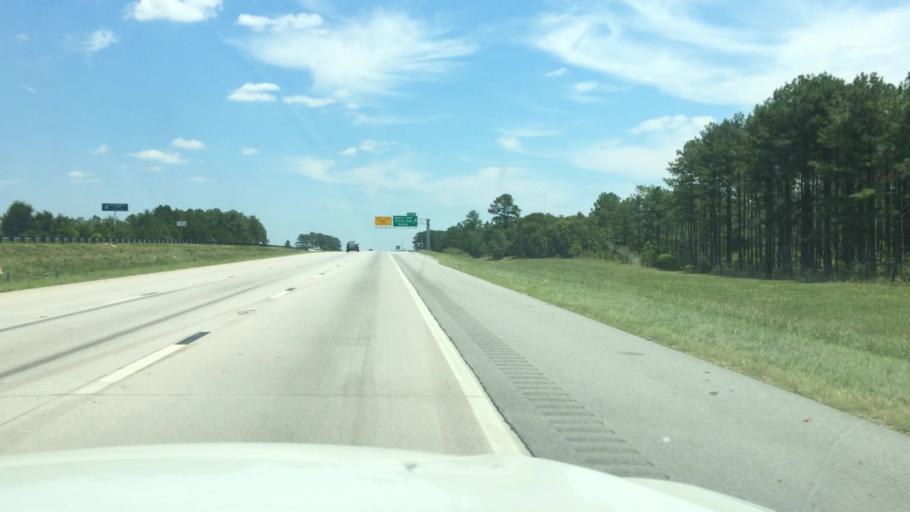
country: US
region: South Carolina
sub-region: Kershaw County
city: Elgin
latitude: 34.1023
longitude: -80.8356
